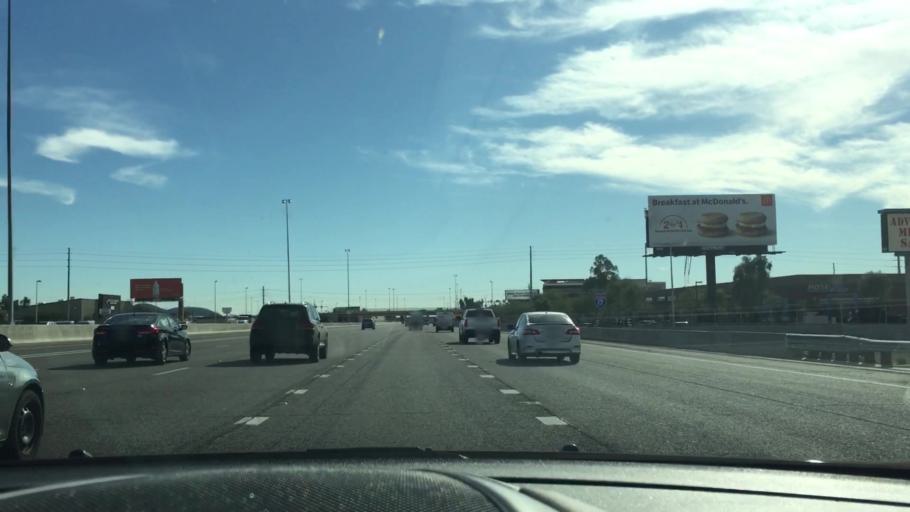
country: US
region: Arizona
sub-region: Maricopa County
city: Glendale
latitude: 33.6817
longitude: -112.1115
